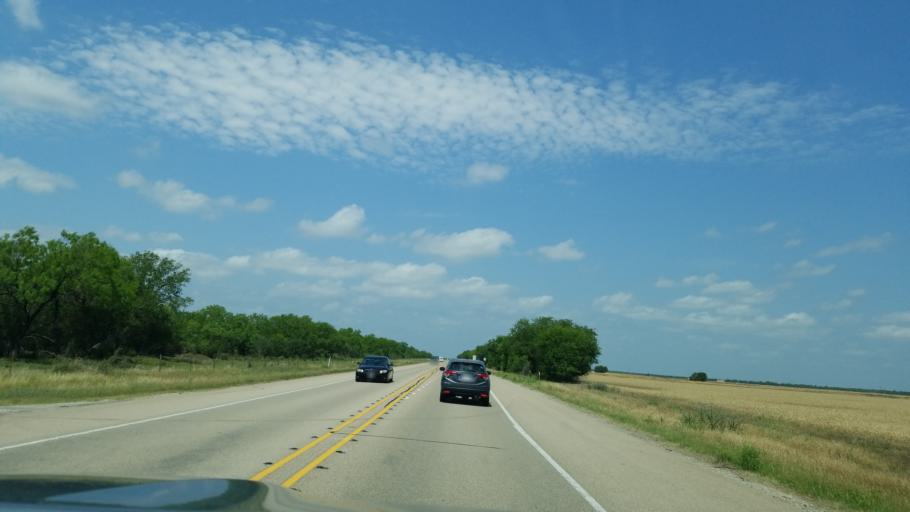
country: US
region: Texas
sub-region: Frio County
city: Pearsall
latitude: 29.0068
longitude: -99.1591
